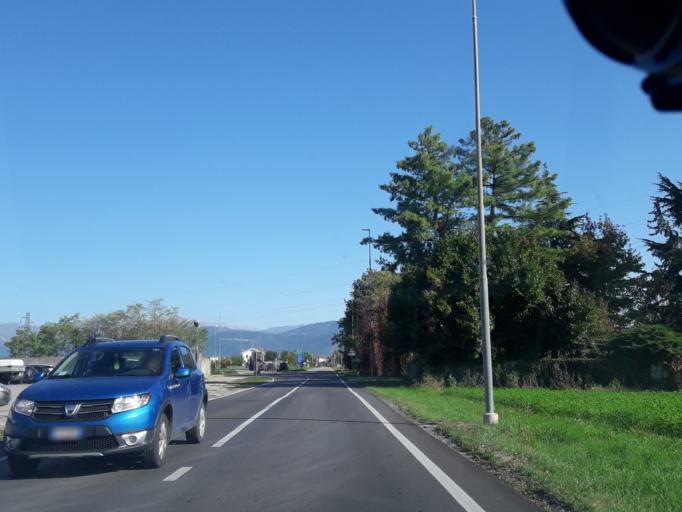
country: IT
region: Friuli Venezia Giulia
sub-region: Provincia di Udine
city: Udine
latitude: 46.0925
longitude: 13.2529
